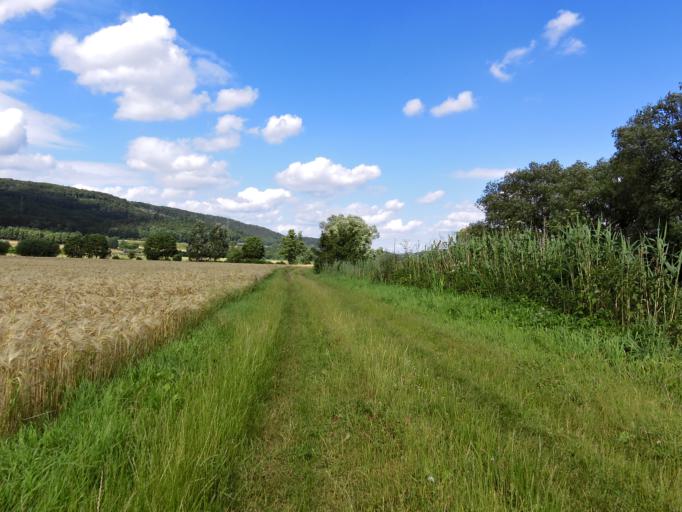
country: DE
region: Hesse
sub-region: Regierungsbezirk Kassel
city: Herleshausen
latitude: 50.9989
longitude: 10.1849
